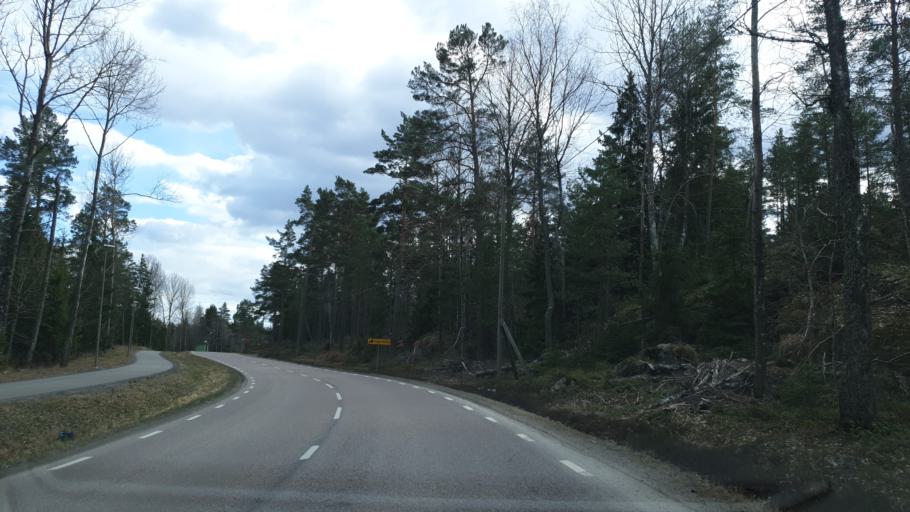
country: SE
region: Stockholm
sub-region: Varmdo Kommun
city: Mortnas
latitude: 59.2754
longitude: 18.4245
